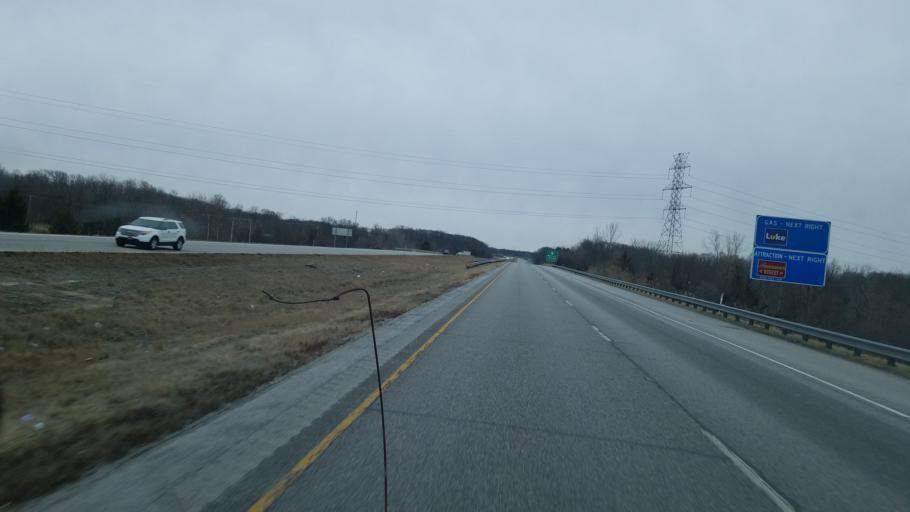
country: US
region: Indiana
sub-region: Porter County
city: Chesterton
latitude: 41.5665
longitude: -87.0467
